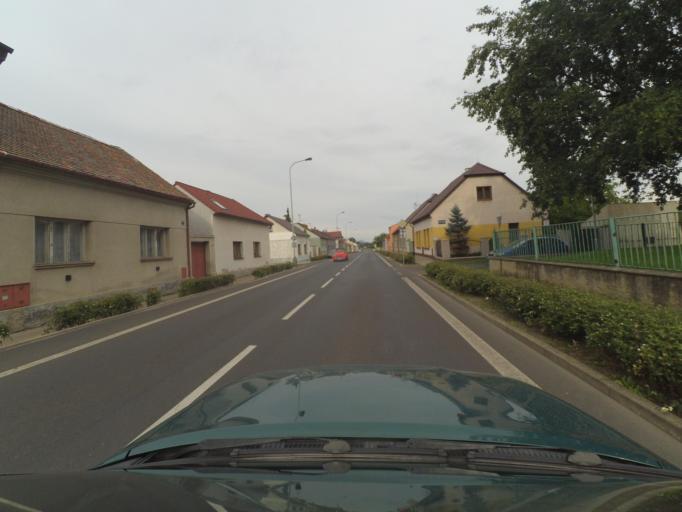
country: CZ
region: Ustecky
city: Cerncice
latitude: 50.3625
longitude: 13.8479
